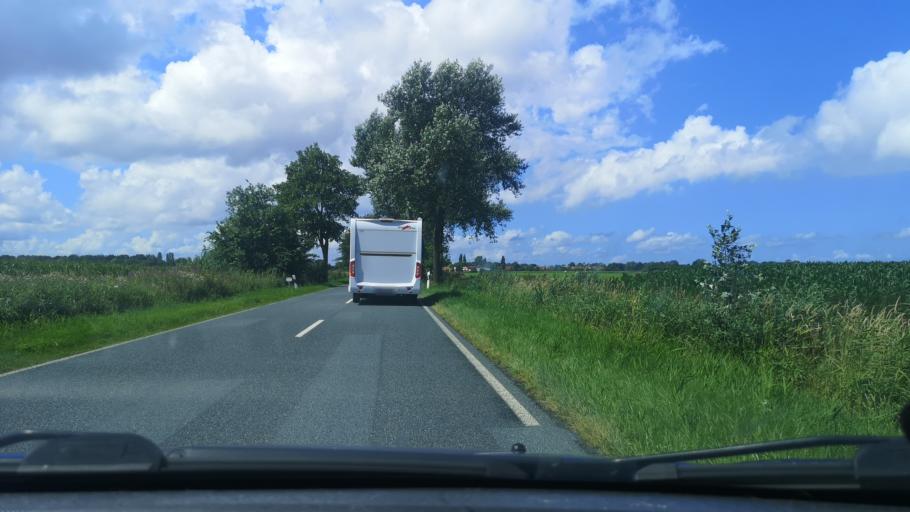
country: DE
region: Lower Saxony
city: Wremen
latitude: 53.6473
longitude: 8.5324
